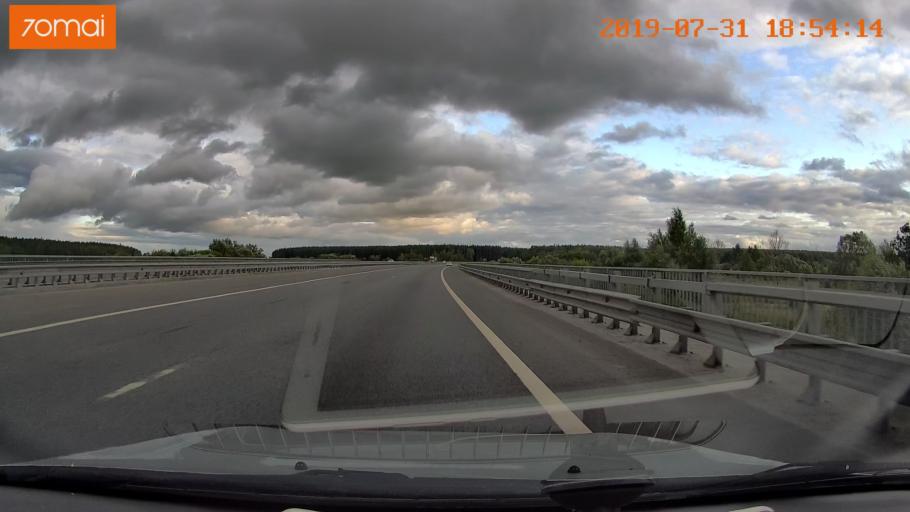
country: RU
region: Moskovskaya
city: Raduzhnyy
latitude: 55.1930
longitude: 38.6672
